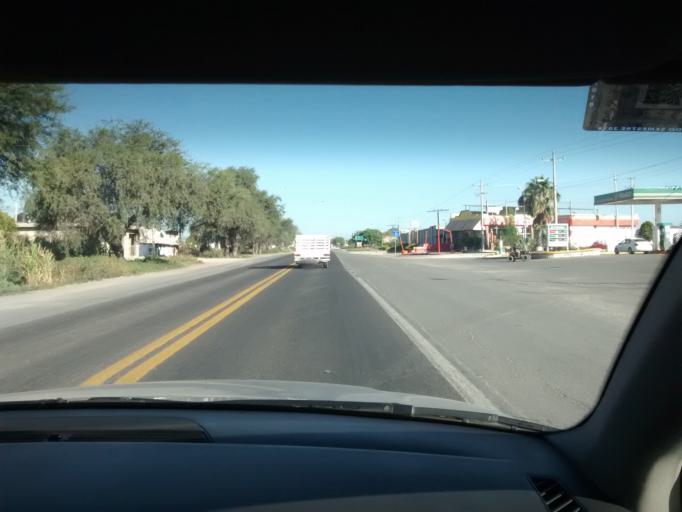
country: MX
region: Puebla
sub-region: Santiago Miahuatlan
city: San Jose Monte Chiquito
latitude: 18.4994
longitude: -97.4749
